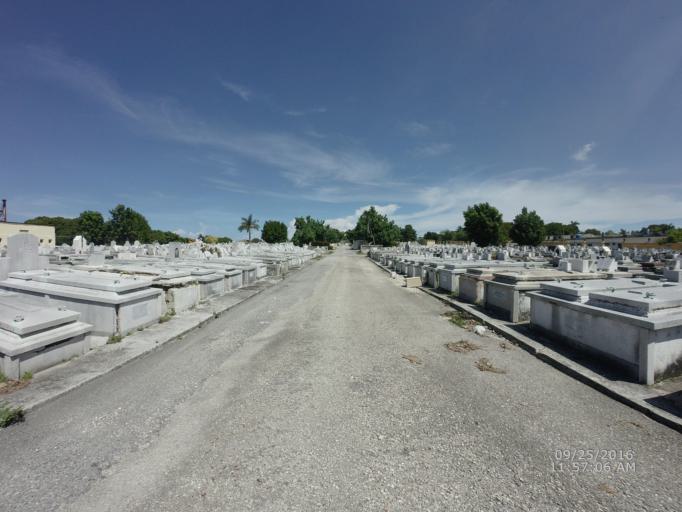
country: CU
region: La Habana
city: Havana
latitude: 23.1206
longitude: -82.3956
